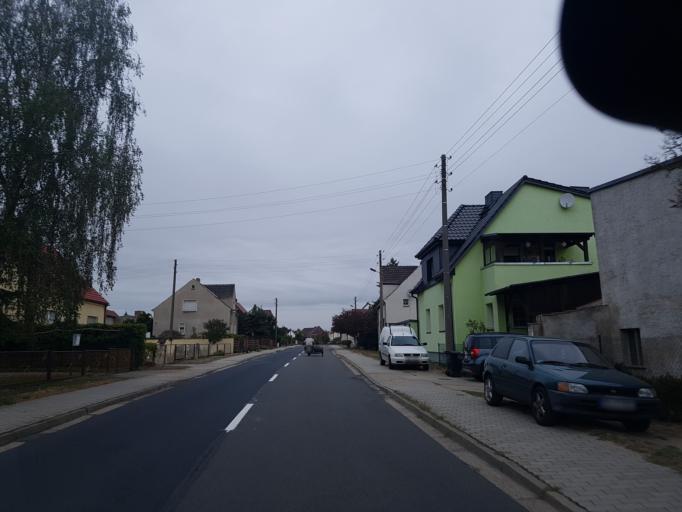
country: DE
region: Saxony-Anhalt
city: Prettin
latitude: 51.6572
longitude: 12.9392
